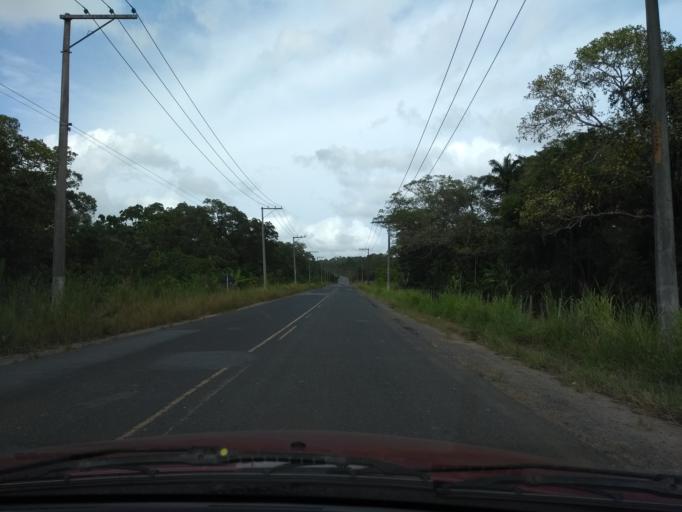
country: BR
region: Bahia
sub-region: Sao Francisco Do Conde
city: Sao Francisco do Conde
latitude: -12.6098
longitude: -38.6471
